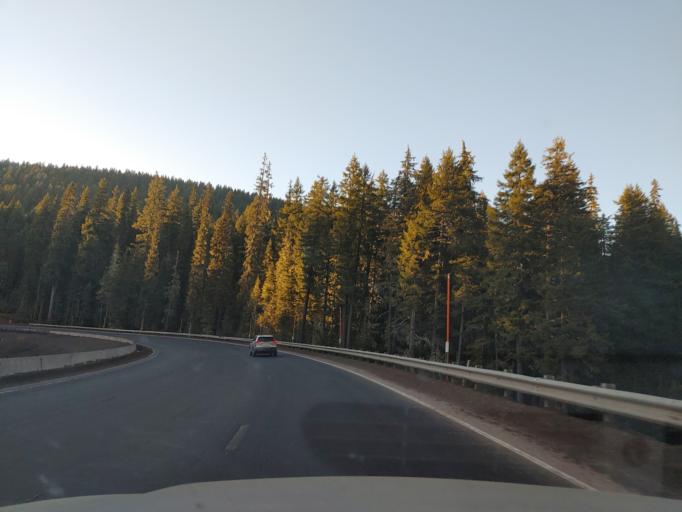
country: US
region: Oregon
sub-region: Lane County
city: Oakridge
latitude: 43.6194
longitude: -122.0674
